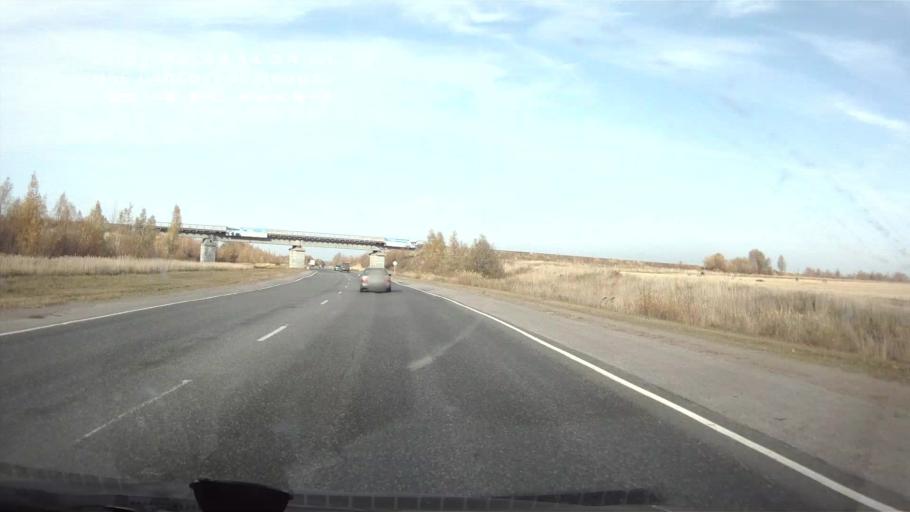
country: RU
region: Chuvashia
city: Kugesi
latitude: 56.0404
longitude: 47.3647
